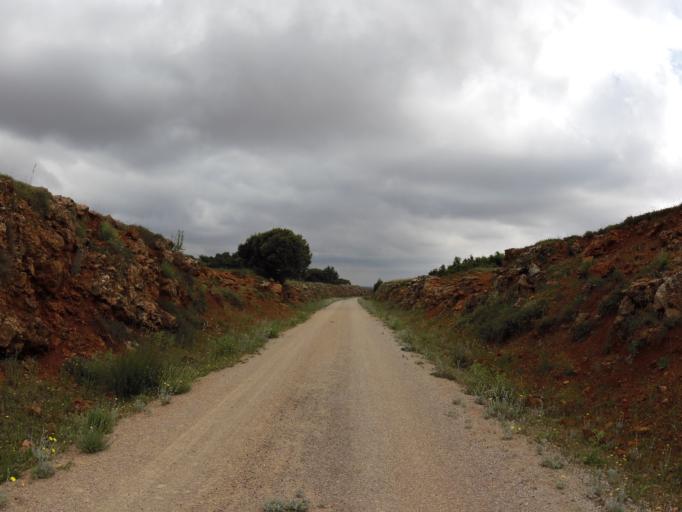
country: ES
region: Castille-La Mancha
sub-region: Provincia de Albacete
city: Robledo
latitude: 38.7573
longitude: -2.4681
